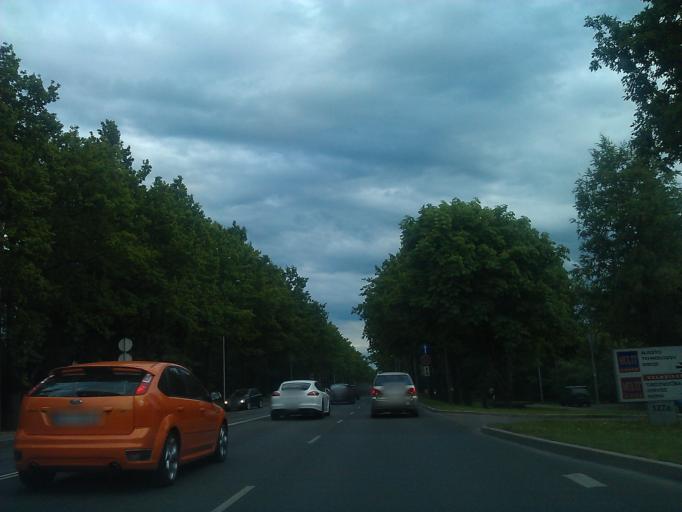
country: LV
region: Marupe
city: Marupe
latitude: 56.9046
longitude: 24.0820
